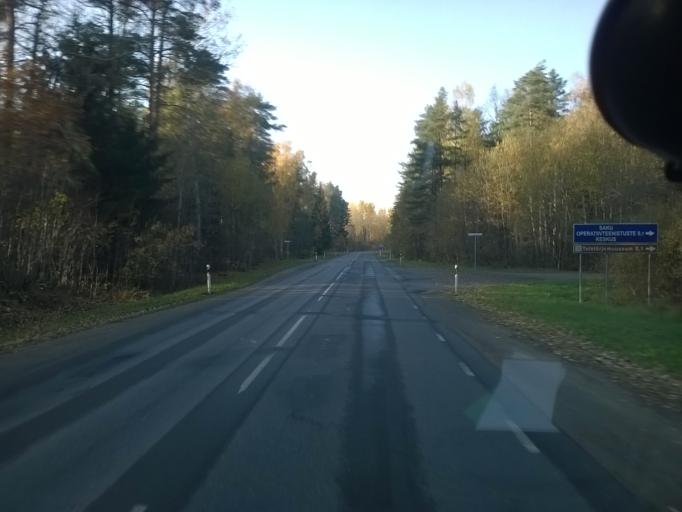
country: EE
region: Harju
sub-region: Saku vald
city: Saku
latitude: 59.3119
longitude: 24.6775
